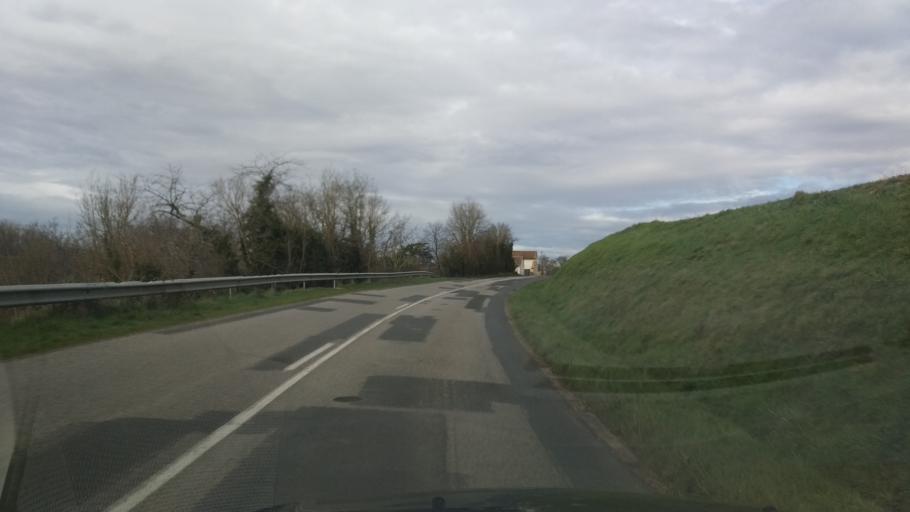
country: FR
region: Poitou-Charentes
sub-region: Departement de la Vienne
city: Chasseneuil-du-Poitou
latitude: 46.6577
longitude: 0.3896
